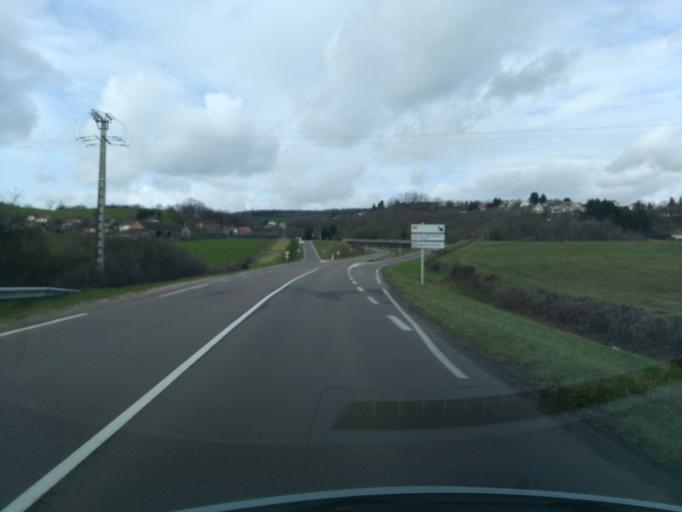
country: FR
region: Bourgogne
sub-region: Departement de Saone-et-Loire
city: Montcenis
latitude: 46.7872
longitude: 4.4041
